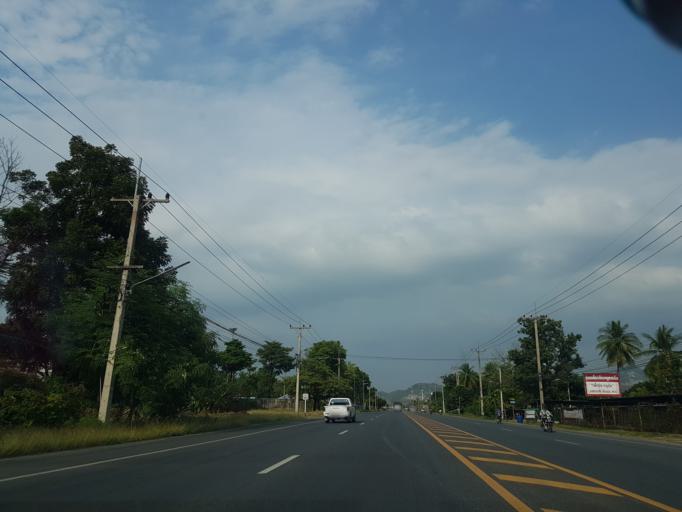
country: TH
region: Sara Buri
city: Ban Mo
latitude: 14.6580
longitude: 100.7654
